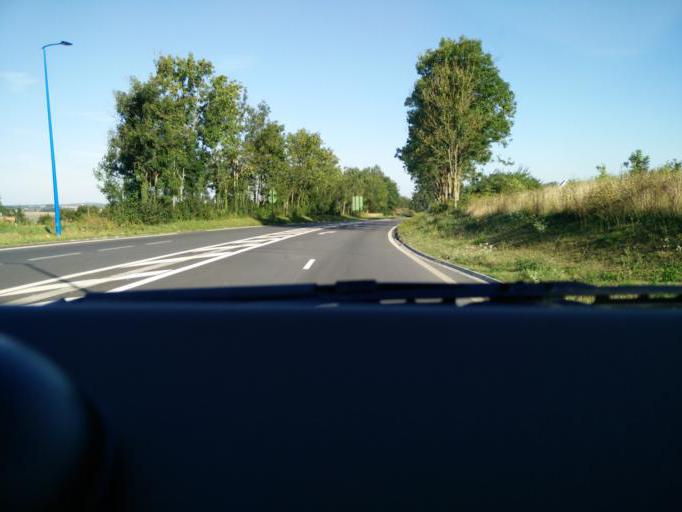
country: FR
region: Nord-Pas-de-Calais
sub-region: Departement du Pas-de-Calais
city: Houdain
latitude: 50.4534
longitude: 2.5443
